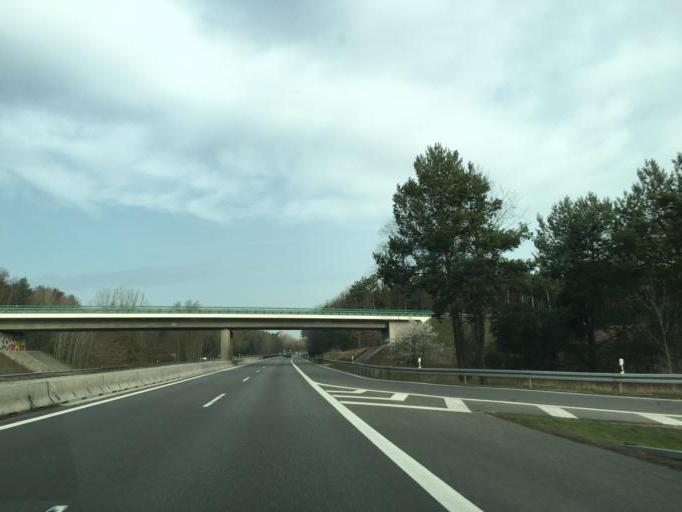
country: DE
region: Brandenburg
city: Fehrbellin
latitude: 52.7667
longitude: 12.8207
